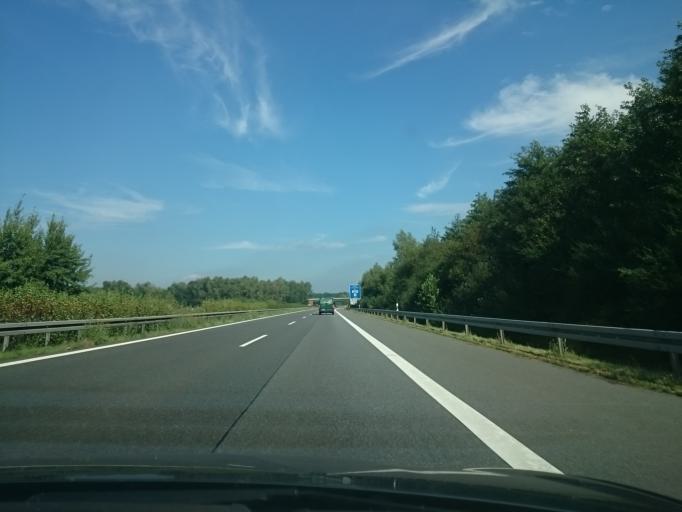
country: DE
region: Brandenburg
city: Schipkau
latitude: 51.5458
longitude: 13.9108
